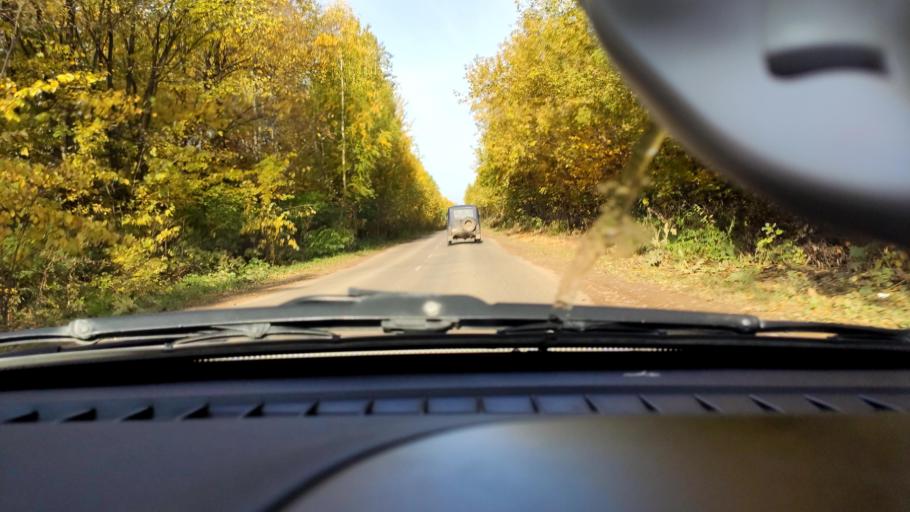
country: RU
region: Perm
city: Overyata
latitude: 58.0659
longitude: 55.8886
